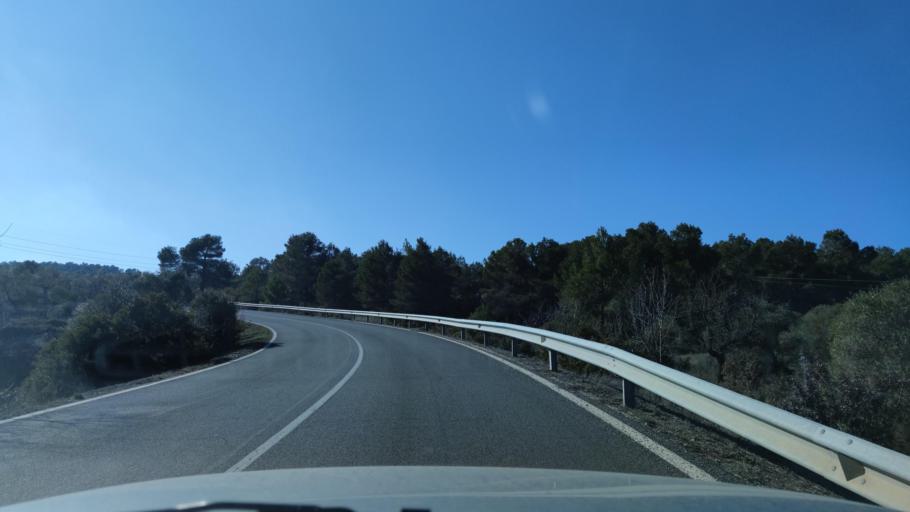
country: ES
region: Catalonia
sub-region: Provincia de Lleida
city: Maials
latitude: 41.3385
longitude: 0.4612
